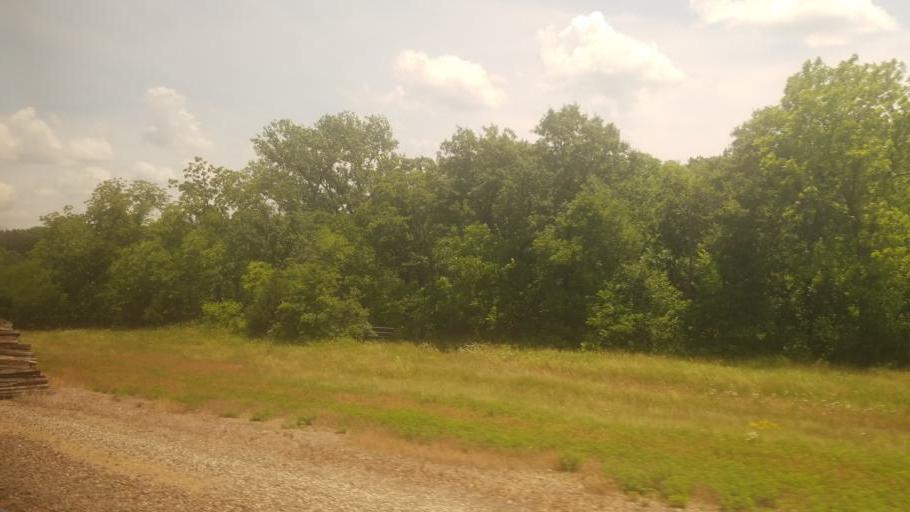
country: US
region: Missouri
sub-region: Macon County
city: La Plata
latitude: 40.0750
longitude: -92.4388
